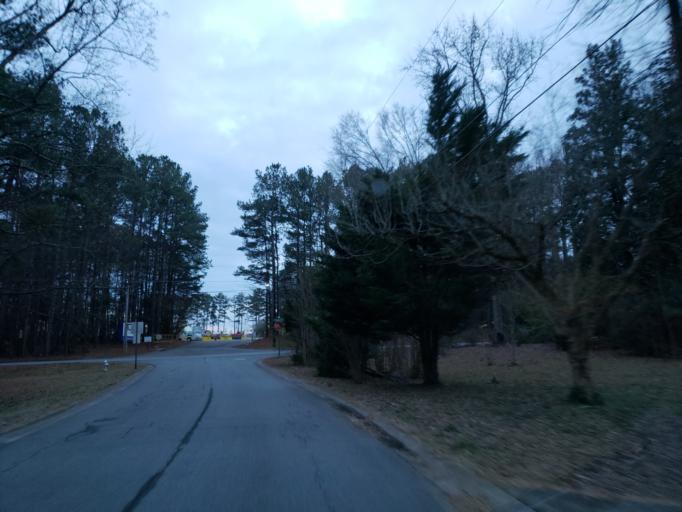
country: US
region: Georgia
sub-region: Cobb County
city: Kennesaw
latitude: 34.0199
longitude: -84.6070
